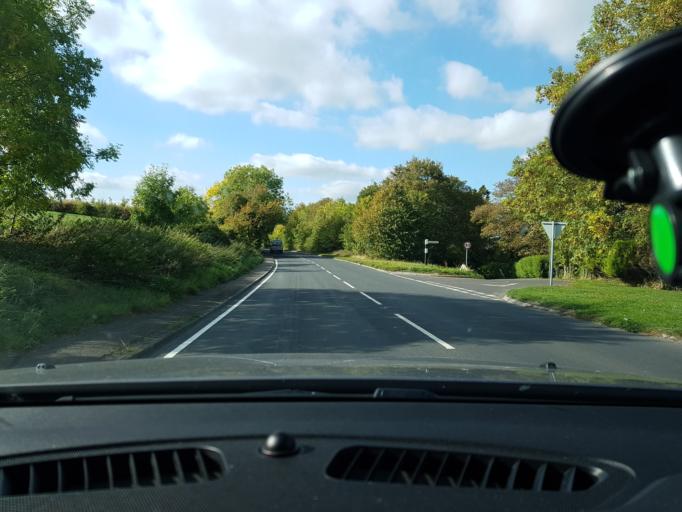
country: GB
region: England
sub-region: Borough of Swindon
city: Wanborough
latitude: 51.5295
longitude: -1.6965
